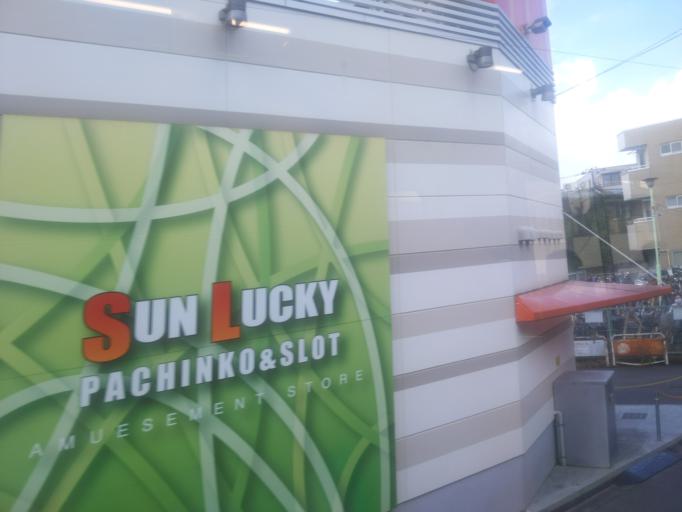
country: JP
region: Tokyo
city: Tokyo
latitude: 35.7200
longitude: 139.6522
